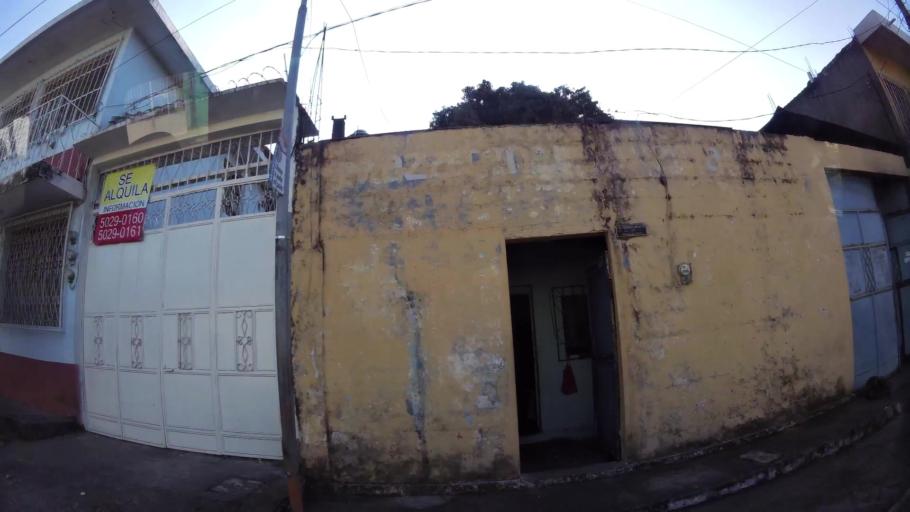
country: GT
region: Suchitepeque
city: Mazatenango
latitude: 14.5319
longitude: -91.5163
